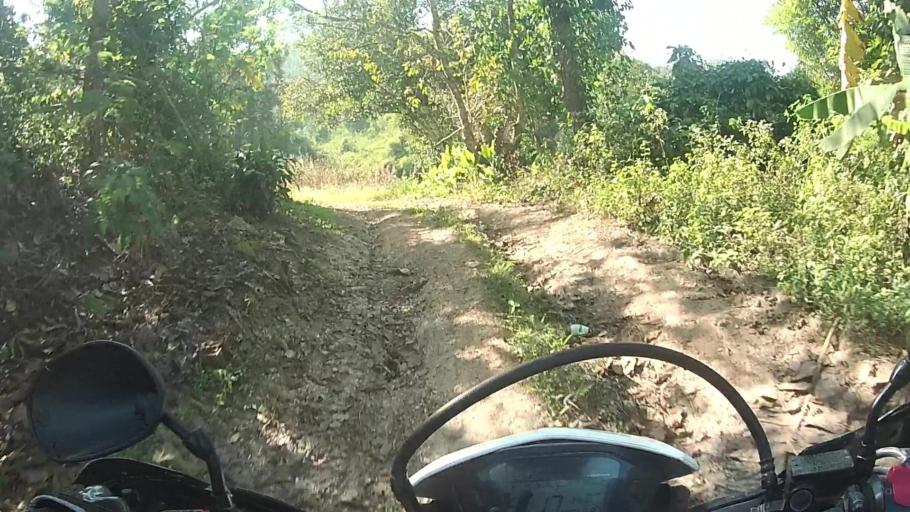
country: TH
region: Chiang Mai
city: San Sai
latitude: 18.9376
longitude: 99.1795
